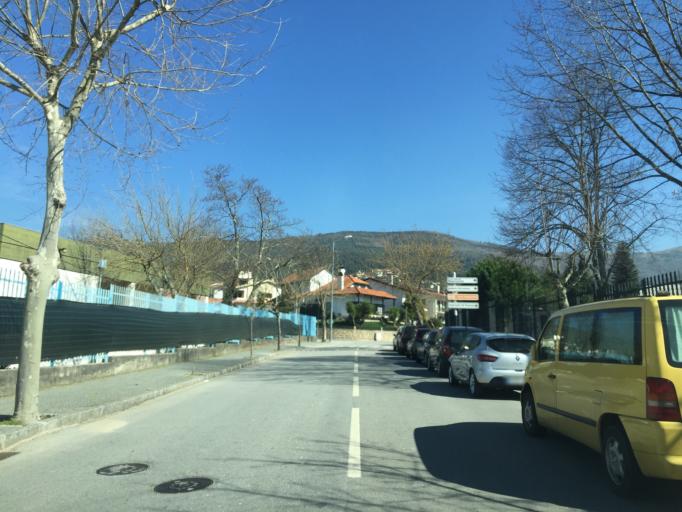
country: PT
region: Aveiro
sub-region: Arouca
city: Arouca
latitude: 40.9296
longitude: -8.2514
